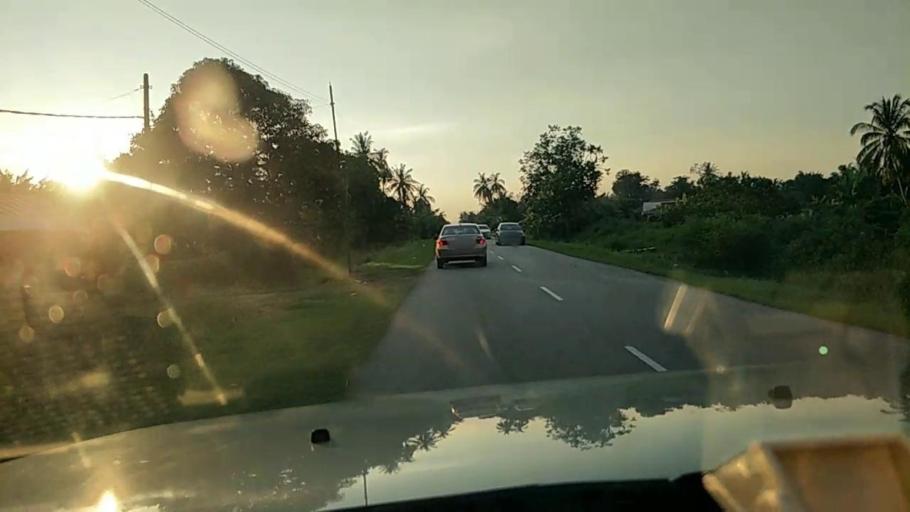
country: MY
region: Selangor
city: Kuala Selangor
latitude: 3.3107
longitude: 101.2884
